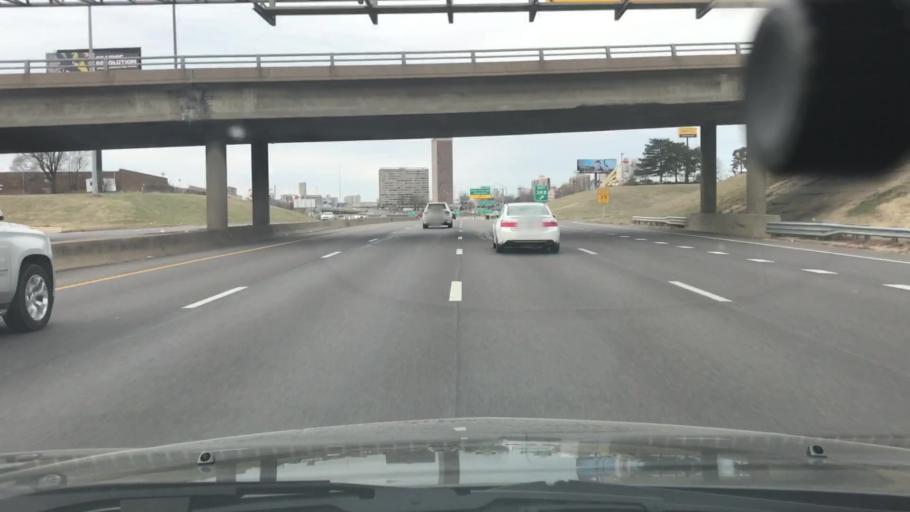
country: US
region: Missouri
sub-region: City of Saint Louis
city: St. Louis
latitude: 38.6290
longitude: -90.2218
